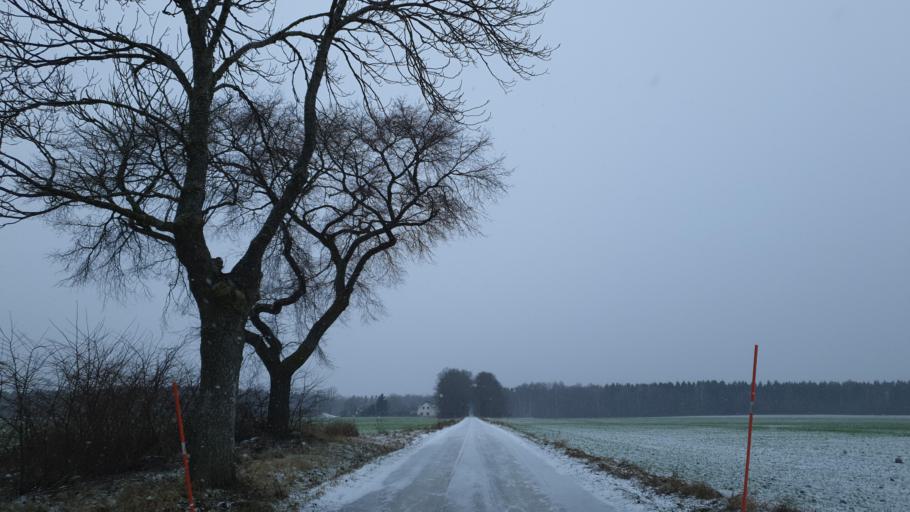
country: SE
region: Gotland
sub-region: Gotland
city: Visby
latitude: 57.5178
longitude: 18.4566
